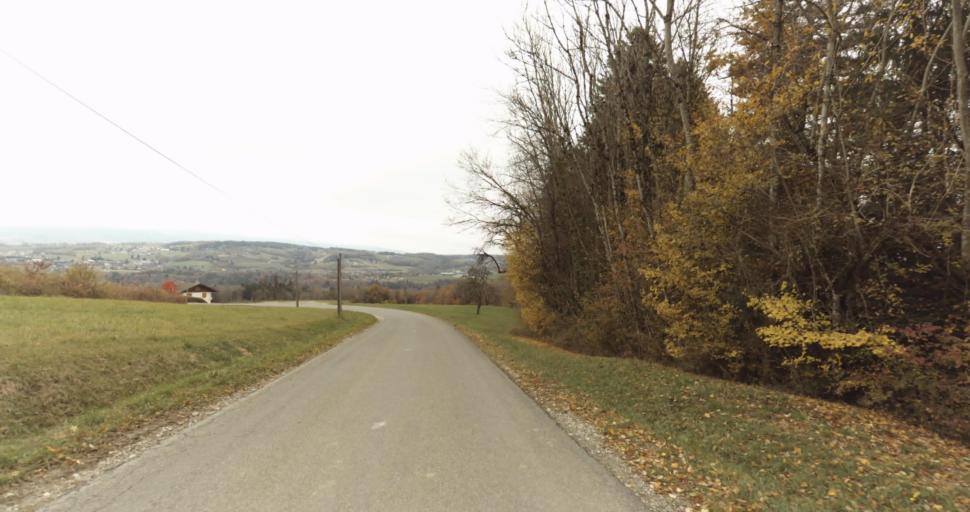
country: FR
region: Rhone-Alpes
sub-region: Departement de la Haute-Savoie
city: Groisy
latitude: 45.9935
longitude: 6.1950
